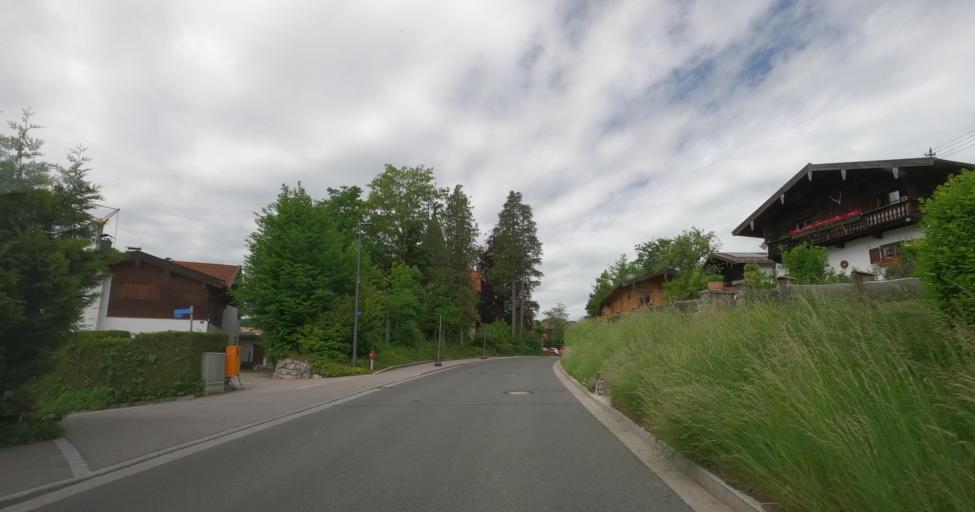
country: DE
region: Bavaria
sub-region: Upper Bavaria
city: Gmund am Tegernsee
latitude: 47.7513
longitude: 11.7332
